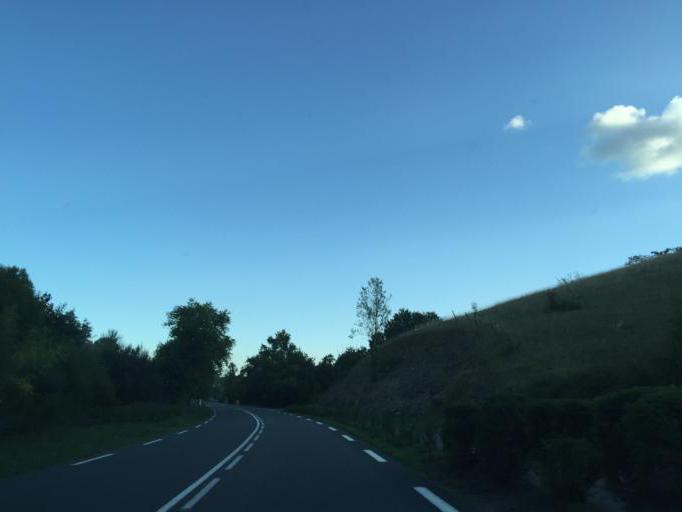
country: FR
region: Midi-Pyrenees
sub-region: Departement de l'Aveyron
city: Rodez
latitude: 44.3882
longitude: 2.5663
